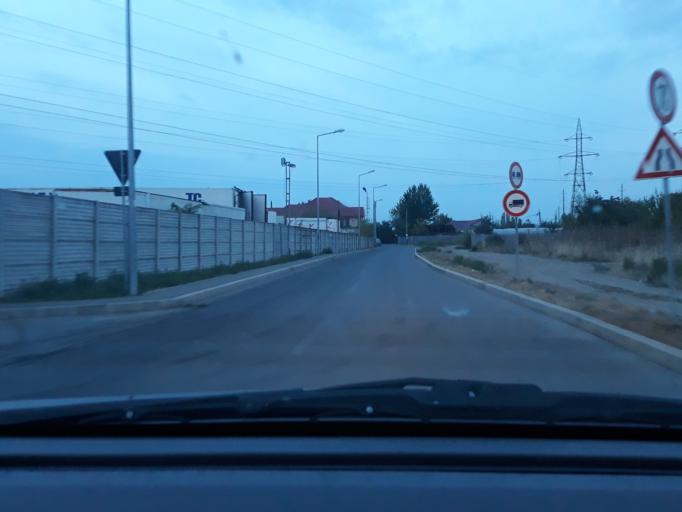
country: RO
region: Bihor
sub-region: Comuna Biharea
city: Oradea
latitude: 47.0353
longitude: 21.9336
